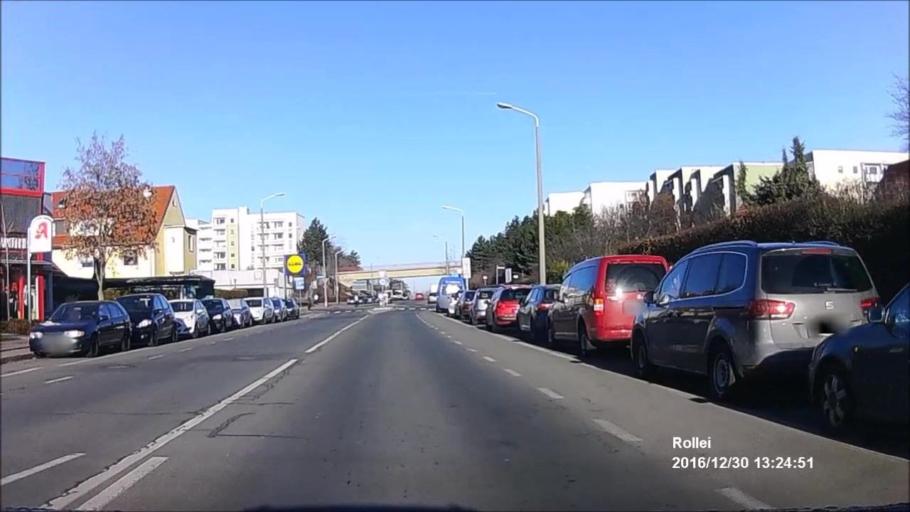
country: DE
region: Thuringia
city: Erfurt
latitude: 50.9571
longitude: 11.0626
